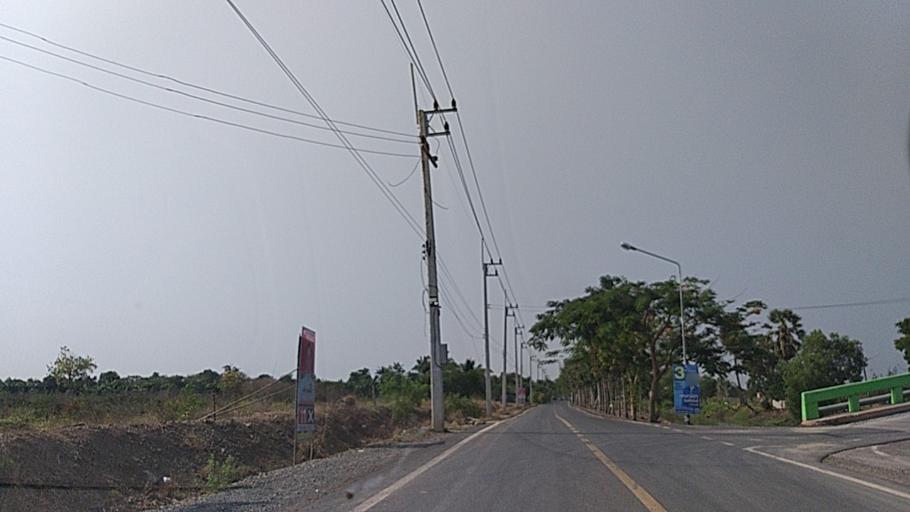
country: TH
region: Pathum Thani
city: Thanyaburi
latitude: 13.9940
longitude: 100.7064
